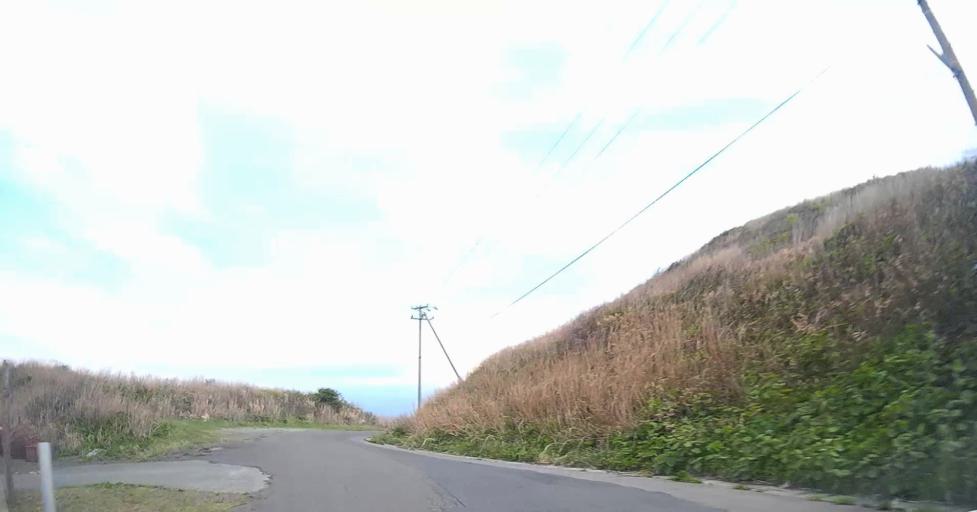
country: JP
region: Aomori
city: Shimokizukuri
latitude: 41.2460
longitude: 140.3436
